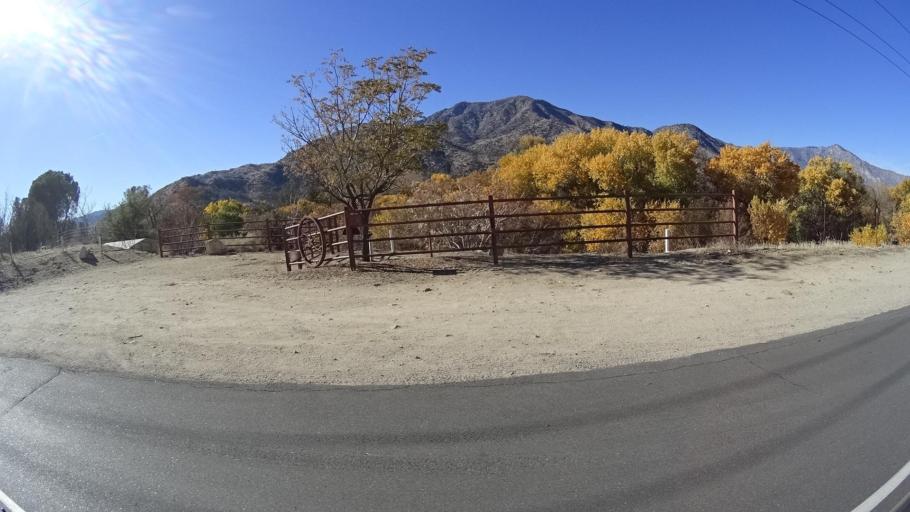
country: US
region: California
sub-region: Kern County
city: Kernville
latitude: 35.7409
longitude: -118.4146
